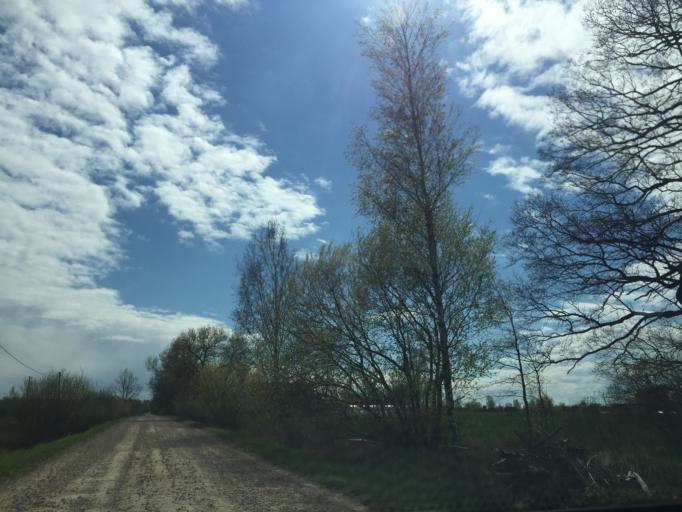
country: LV
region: Jelgava
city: Jelgava
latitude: 56.5669
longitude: 23.7810
